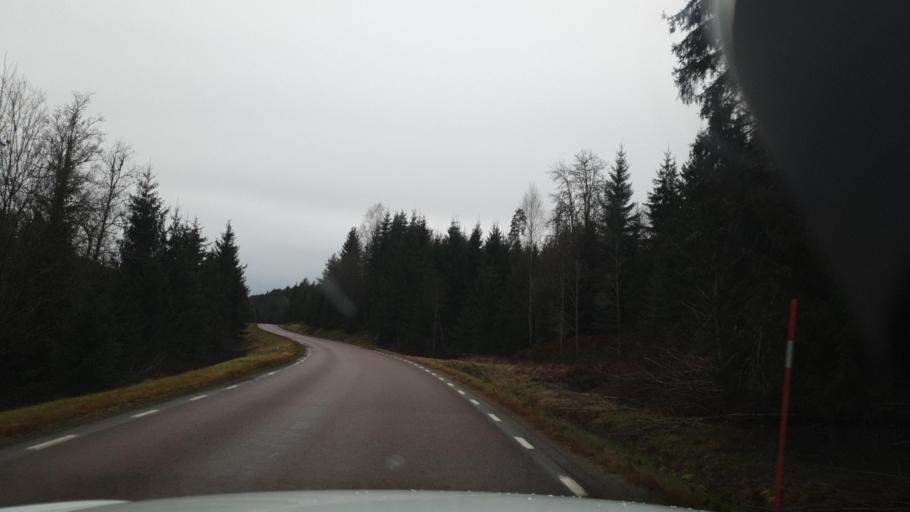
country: SE
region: Vaermland
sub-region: Arvika Kommun
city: Arvika
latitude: 59.7096
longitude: 12.7927
